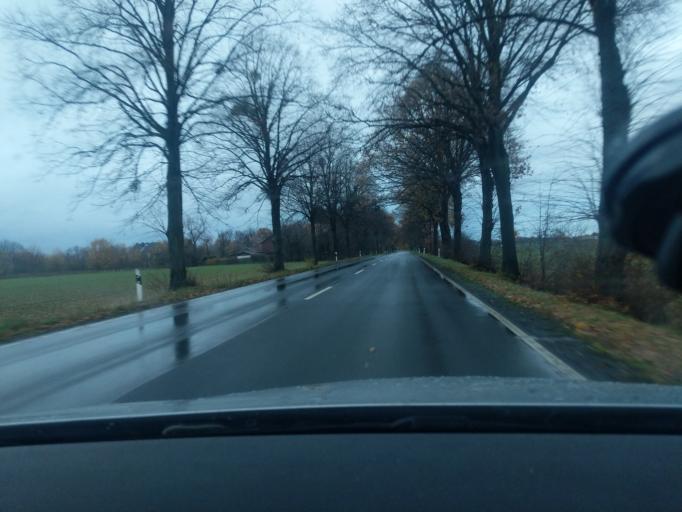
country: DE
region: North Rhine-Westphalia
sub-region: Regierungsbezirk Arnsberg
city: Bonen
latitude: 51.5934
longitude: 7.7930
